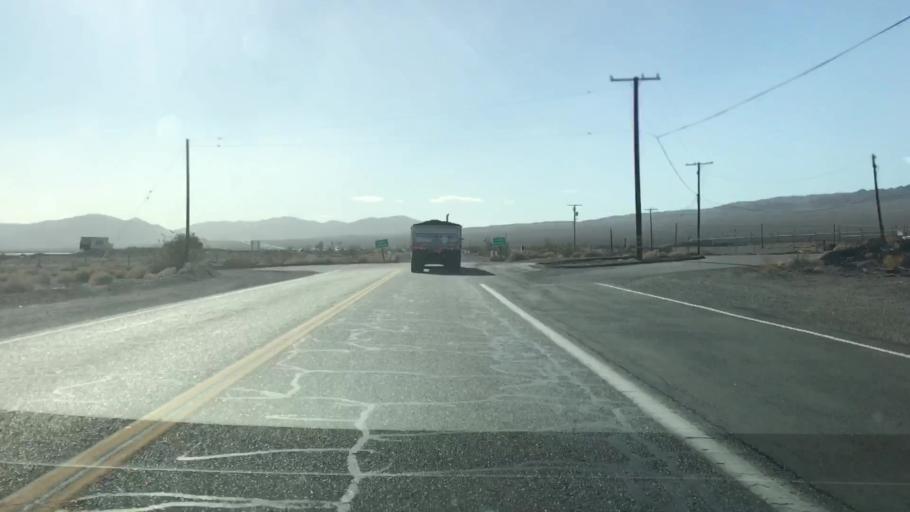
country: US
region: California
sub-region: San Bernardino County
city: Fort Irwin
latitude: 35.2573
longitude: -116.0856
